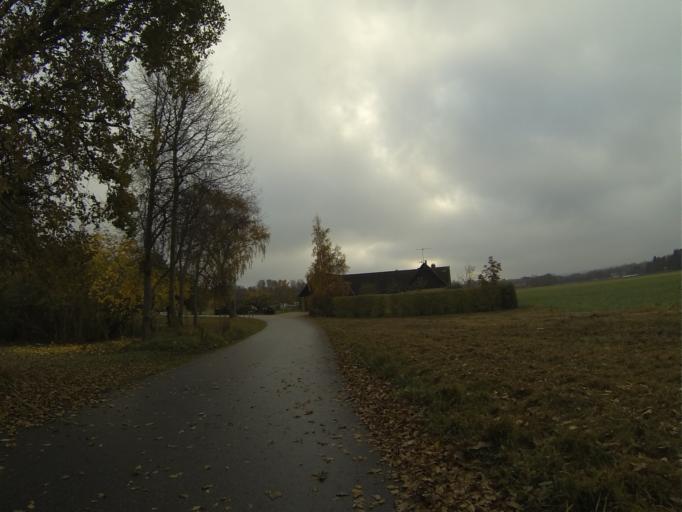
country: SE
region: Skane
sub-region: Hoors Kommun
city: Loberod
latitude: 55.7222
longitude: 13.4057
